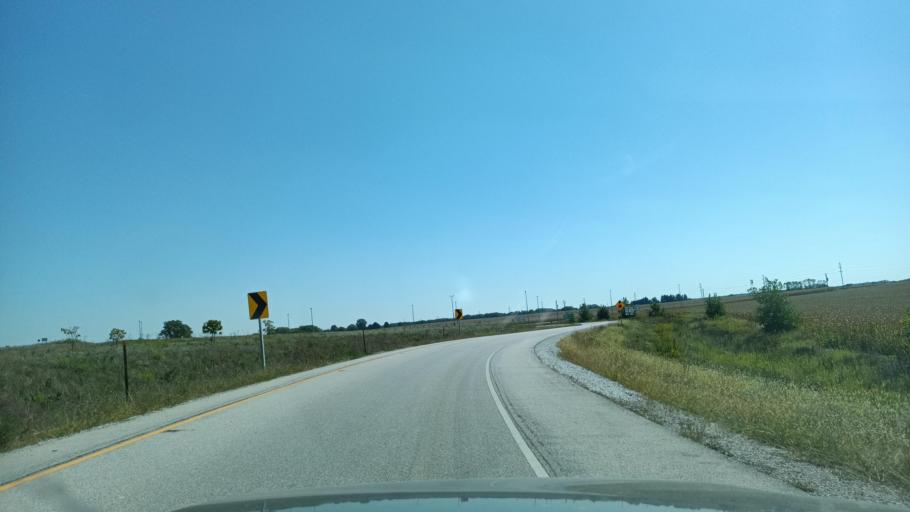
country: US
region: Illinois
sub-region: McDonough County
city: Macomb
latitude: 40.5029
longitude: -90.6778
